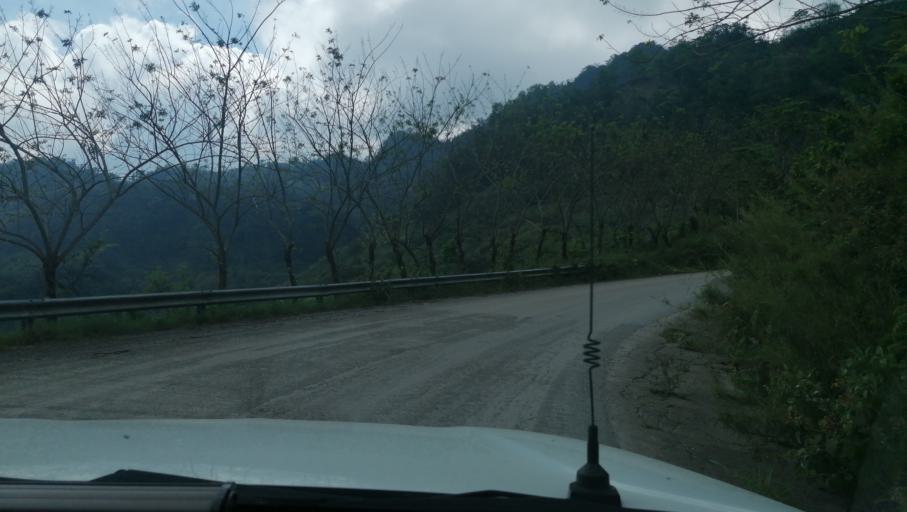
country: MX
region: Chiapas
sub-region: Ocotepec
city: San Pablo Huacano
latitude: 17.2635
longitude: -93.2651
